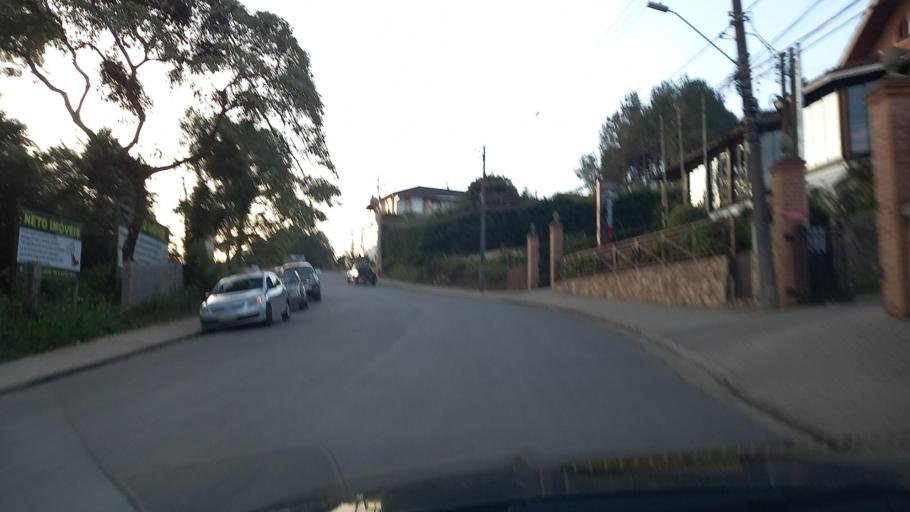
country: BR
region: Minas Gerais
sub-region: Camanducaia
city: Camanducaia
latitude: -22.8612
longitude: -46.0306
